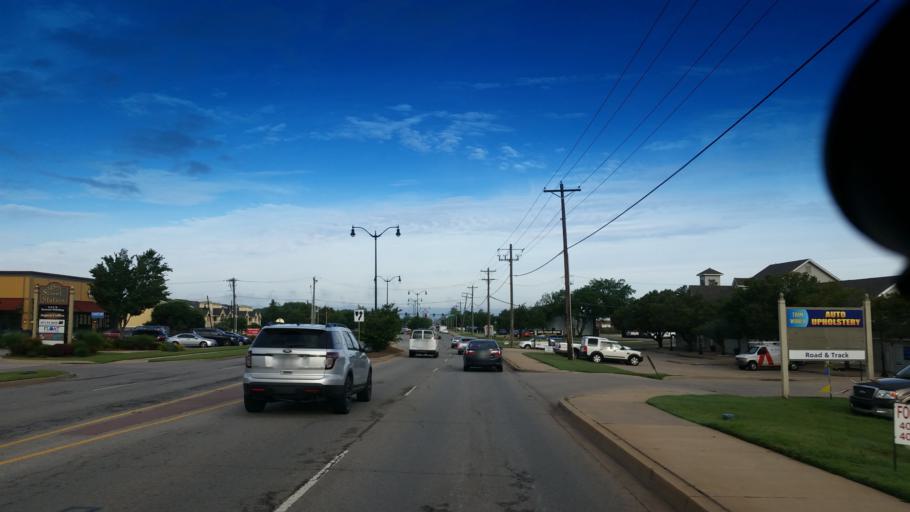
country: US
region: Oklahoma
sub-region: Oklahoma County
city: Edmond
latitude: 35.6384
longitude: -97.4858
